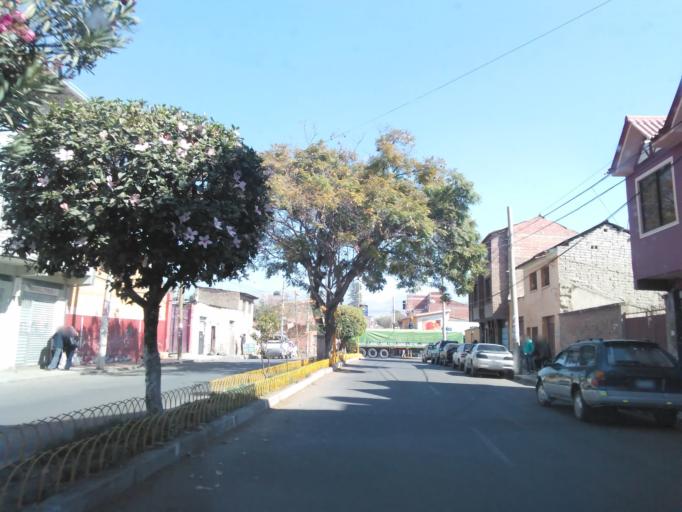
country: BO
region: Cochabamba
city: Sipe Sipe
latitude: -17.3980
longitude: -66.2774
